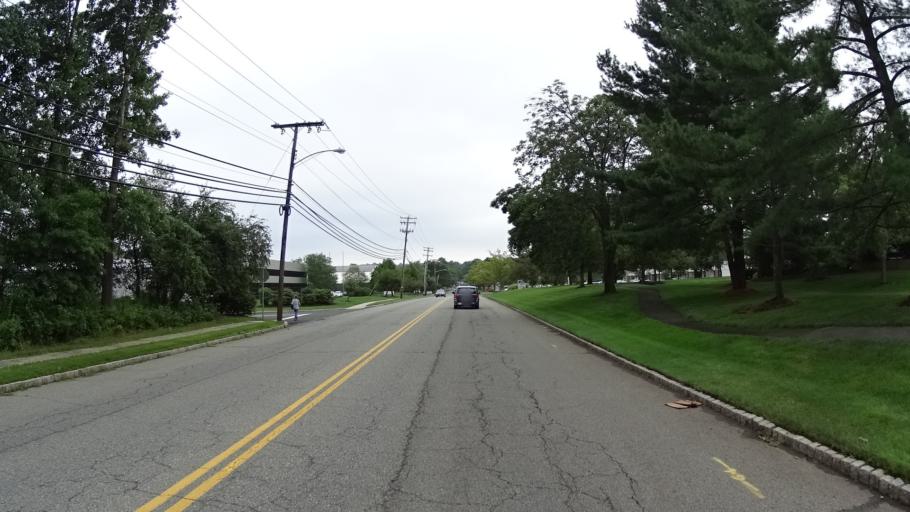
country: US
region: New Jersey
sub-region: Union County
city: New Providence
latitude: 40.6977
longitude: -74.4077
